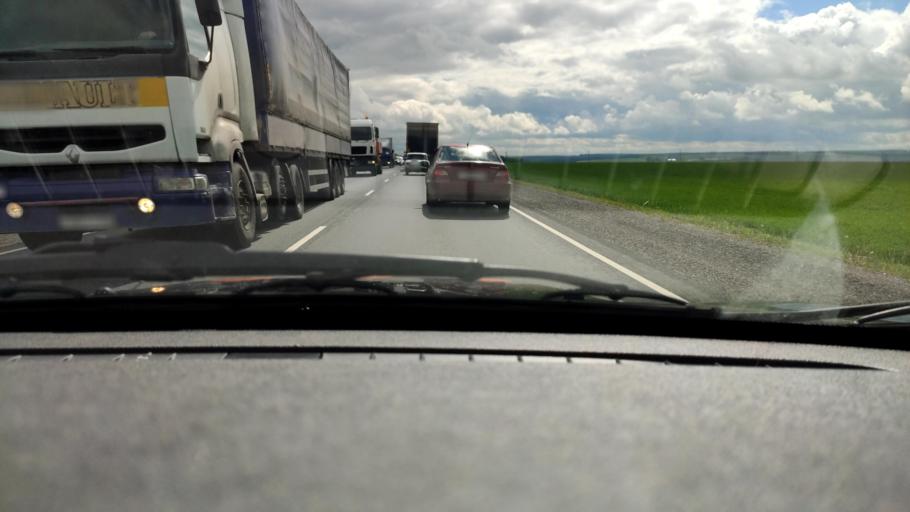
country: RU
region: Voronezj
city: Nizhnedevitsk
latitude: 51.6060
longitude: 38.6078
